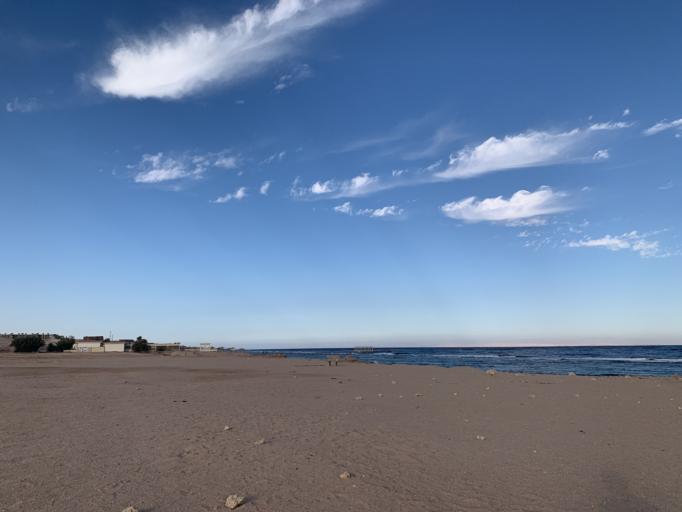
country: EG
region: South Sinai
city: Sharm el-Sheikh
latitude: 28.0009
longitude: 34.4354
